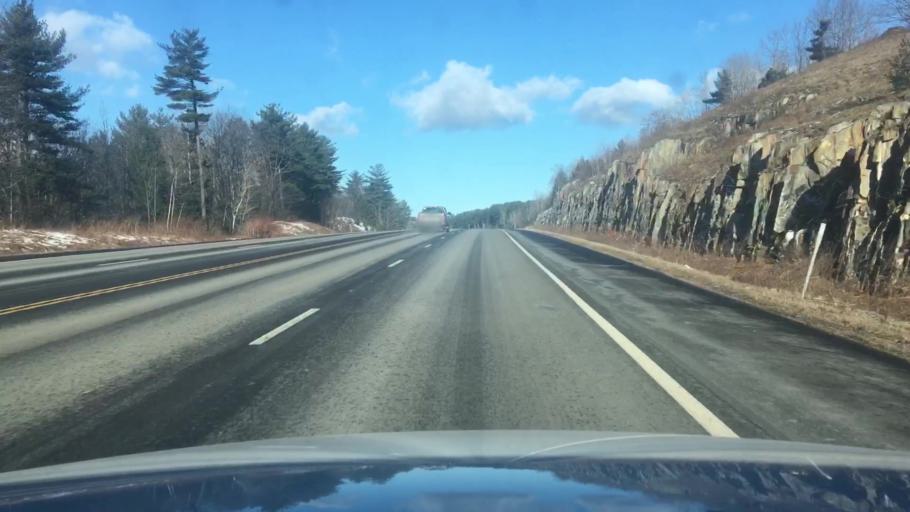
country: US
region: Maine
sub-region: Kennebec County
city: Augusta
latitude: 44.3386
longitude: -69.7670
